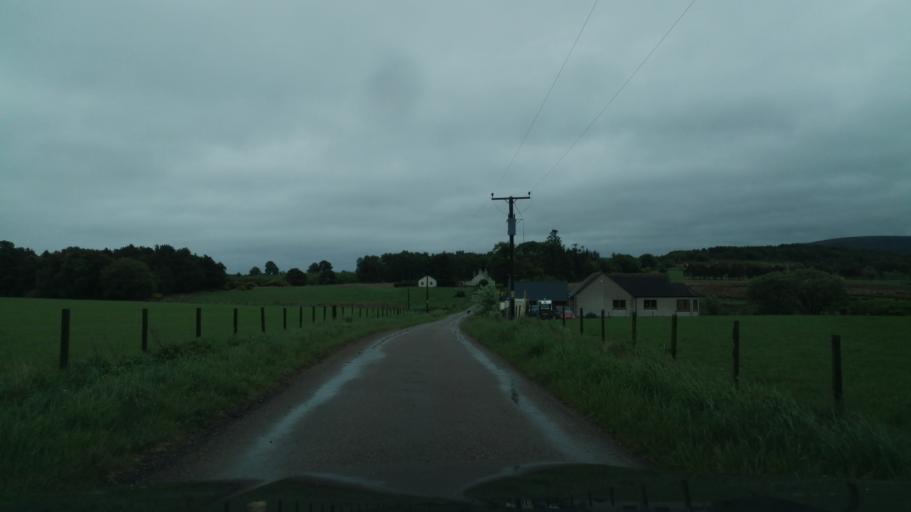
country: GB
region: Scotland
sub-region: Moray
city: Keith
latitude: 57.5699
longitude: -2.8613
